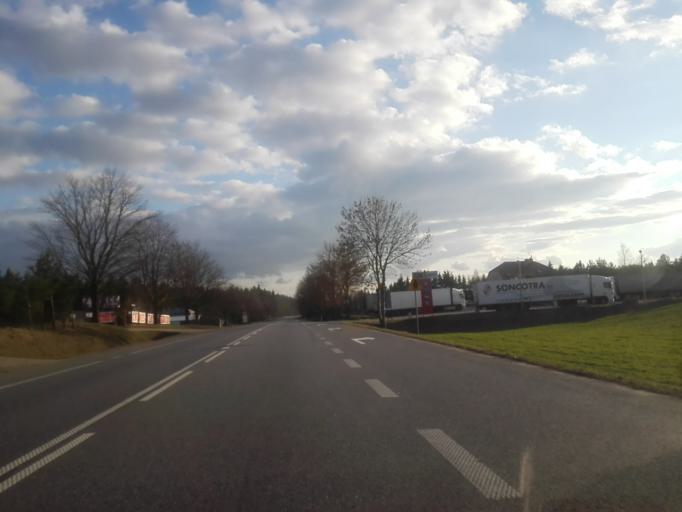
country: PL
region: Podlasie
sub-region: Suwalki
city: Suwalki
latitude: 54.1627
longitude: 22.9812
